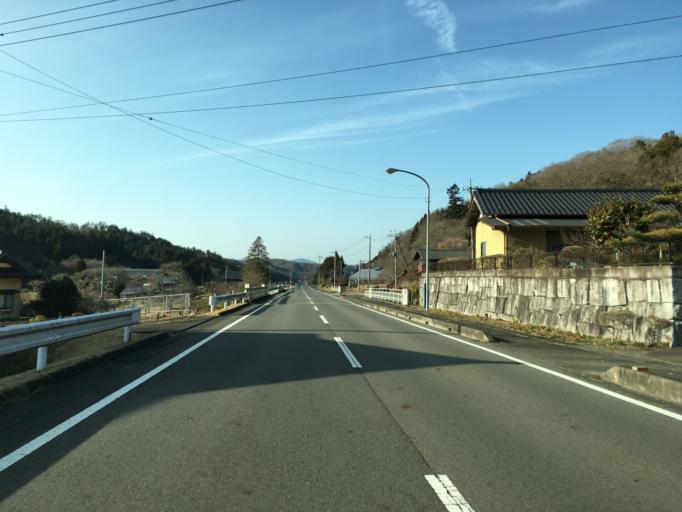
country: JP
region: Ibaraki
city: Daigo
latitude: 36.7530
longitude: 140.4405
